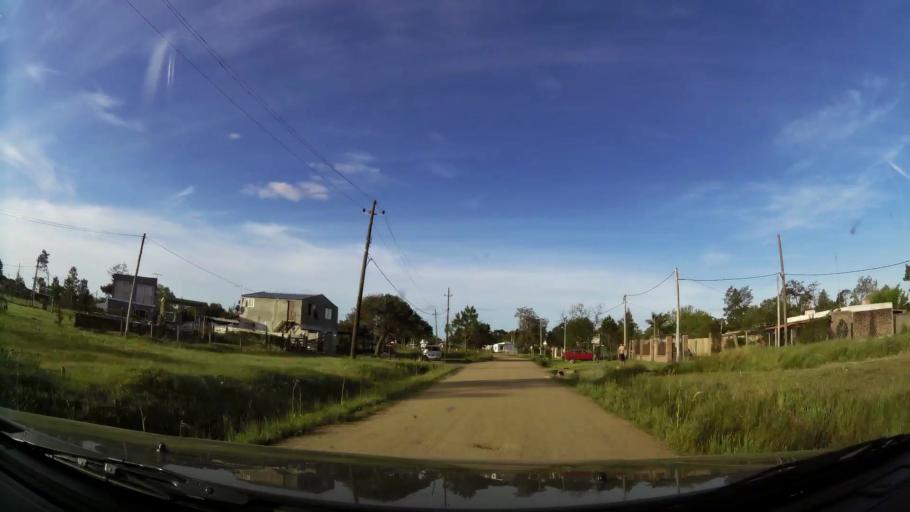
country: UY
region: Canelones
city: Empalme Olmos
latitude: -34.7771
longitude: -55.8613
